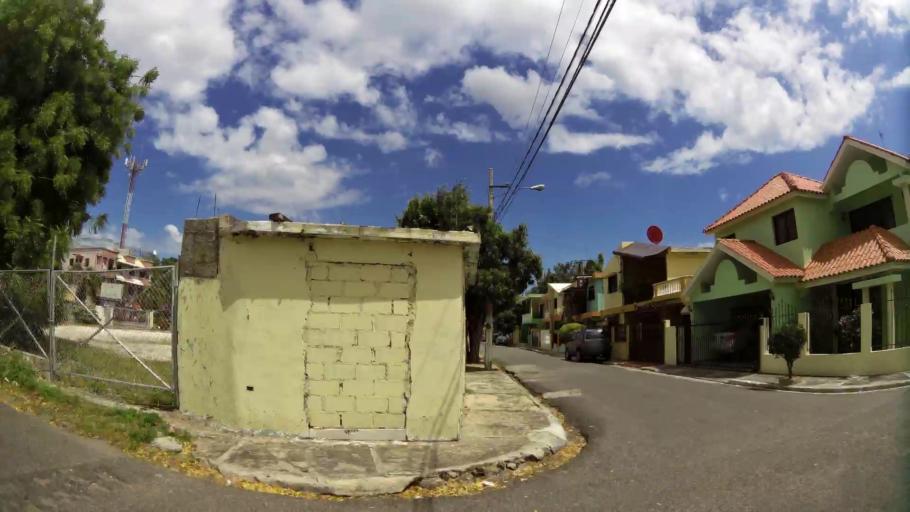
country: DO
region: San Cristobal
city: San Cristobal
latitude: 18.4146
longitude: -70.0992
